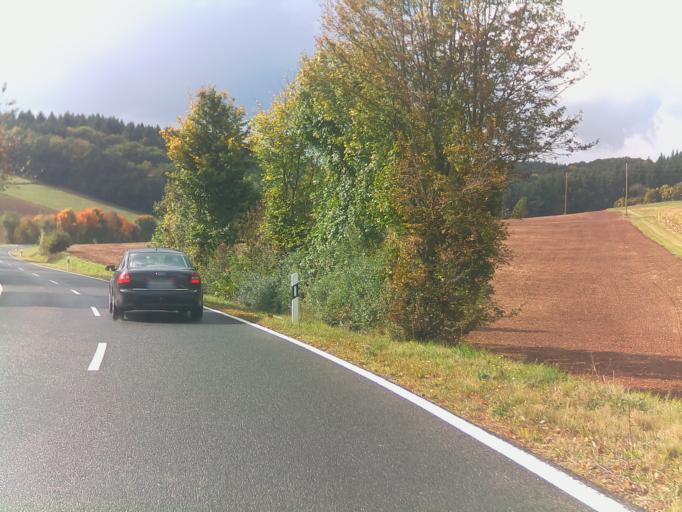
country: DE
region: Baden-Wuerttemberg
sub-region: Regierungsbezirk Stuttgart
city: Werbach
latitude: 49.6734
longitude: 9.6132
